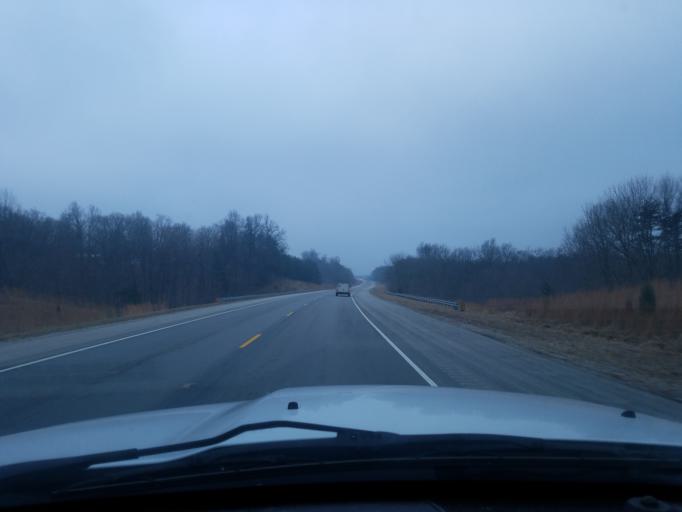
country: US
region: Indiana
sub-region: Perry County
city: Tell City
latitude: 38.0787
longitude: -86.6150
